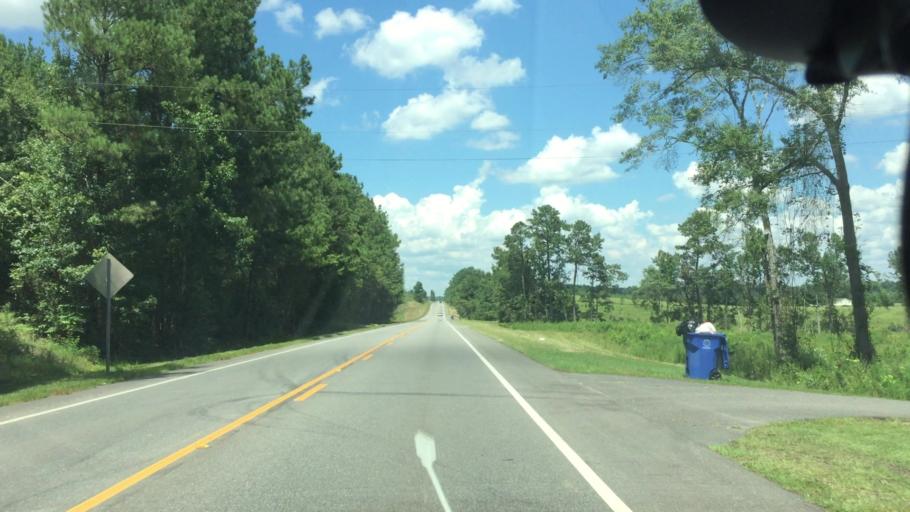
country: US
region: Alabama
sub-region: Pike County
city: Brundidge
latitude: 31.6066
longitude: -85.9466
